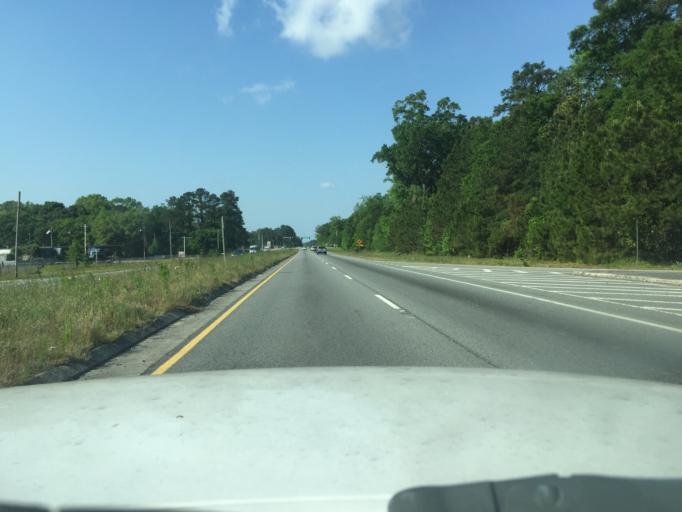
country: US
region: Georgia
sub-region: Chatham County
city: Georgetown
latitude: 32.0323
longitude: -81.2193
